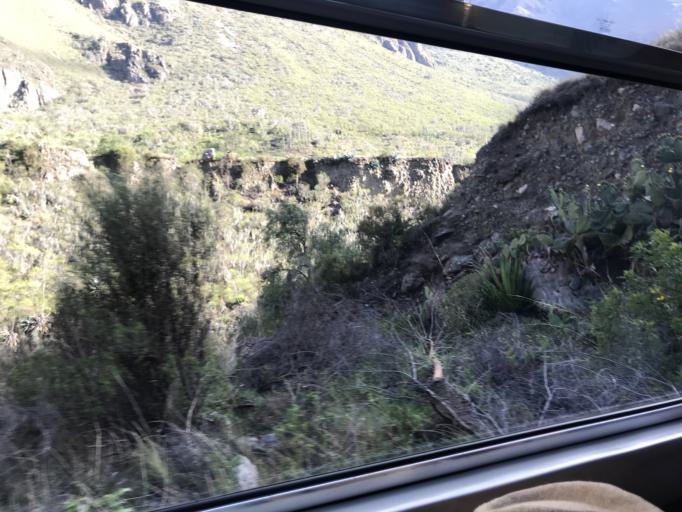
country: PE
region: Cusco
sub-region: Provincia de Urubamba
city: Ollantaytambo
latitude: -13.2206
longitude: -72.3919
